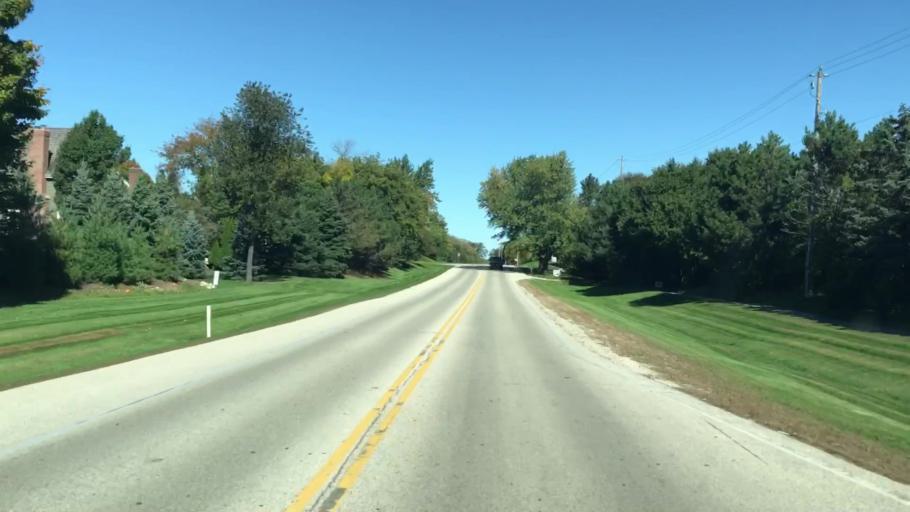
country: US
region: Wisconsin
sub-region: Waukesha County
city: Brookfield
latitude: 43.0645
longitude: -88.1663
